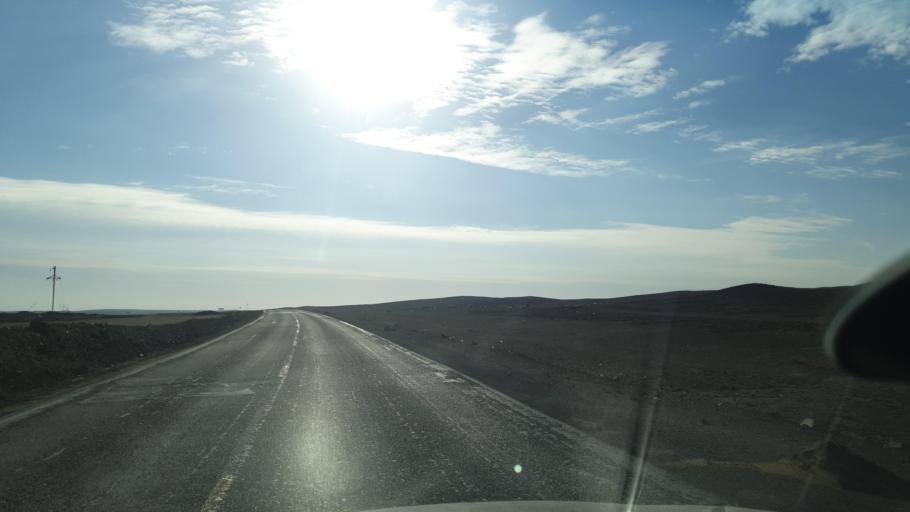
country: KZ
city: Priozersk
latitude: 45.7998
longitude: 73.3902
